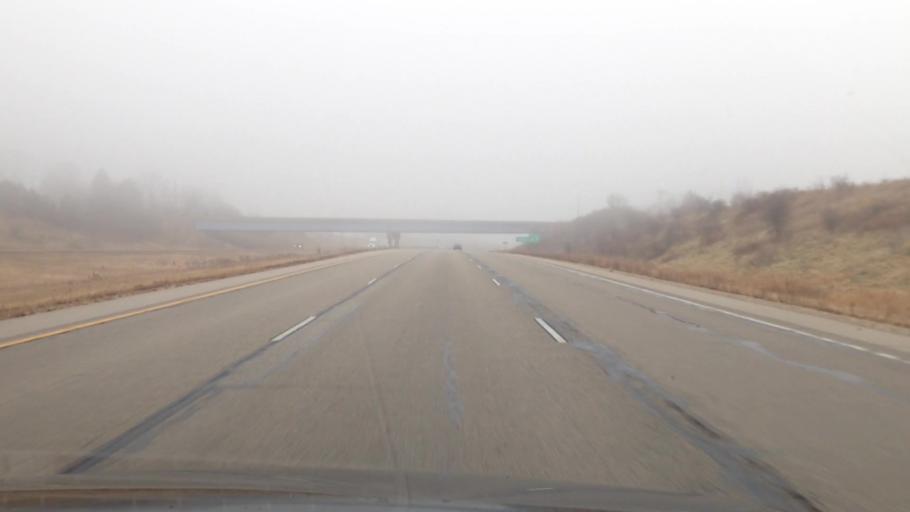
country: US
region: Wisconsin
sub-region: Walworth County
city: East Troy
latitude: 42.7399
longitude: -88.4533
